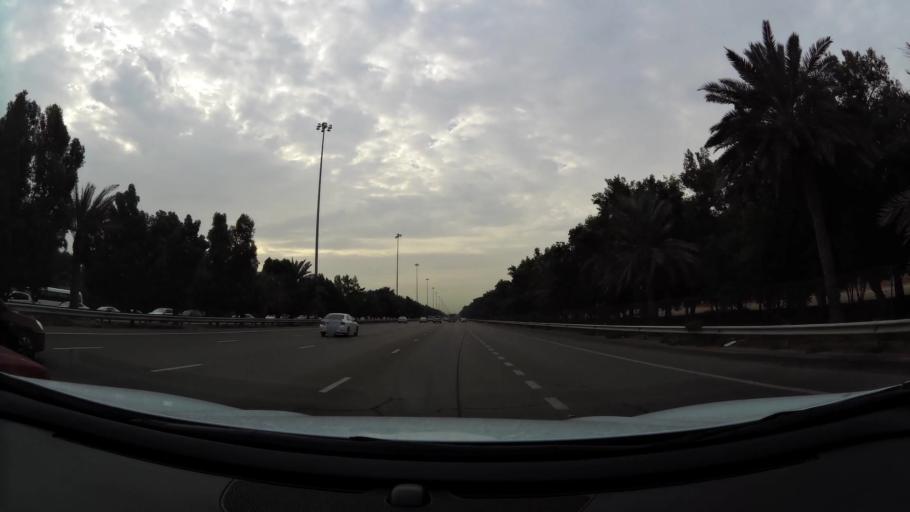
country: AE
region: Abu Dhabi
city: Abu Dhabi
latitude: 24.3453
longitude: 54.5731
